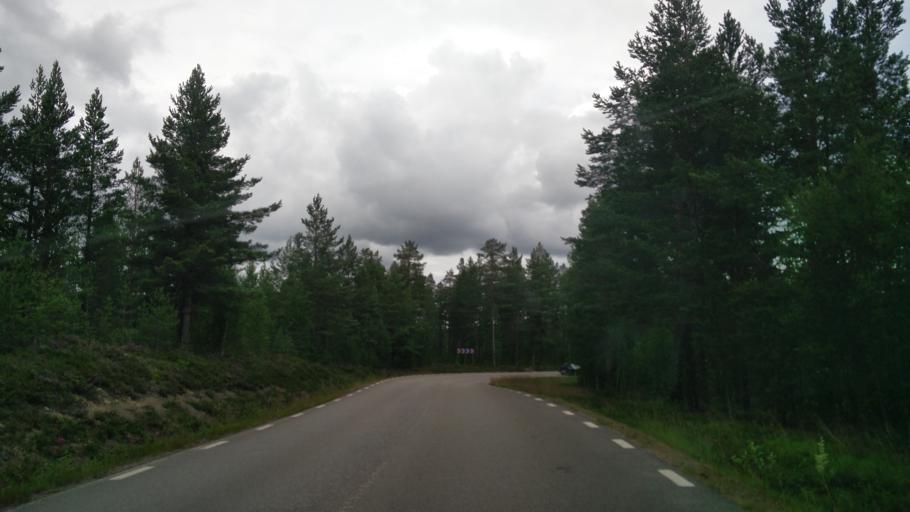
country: NO
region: Hedmark
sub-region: Trysil
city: Innbygda
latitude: 61.1705
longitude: 12.8406
